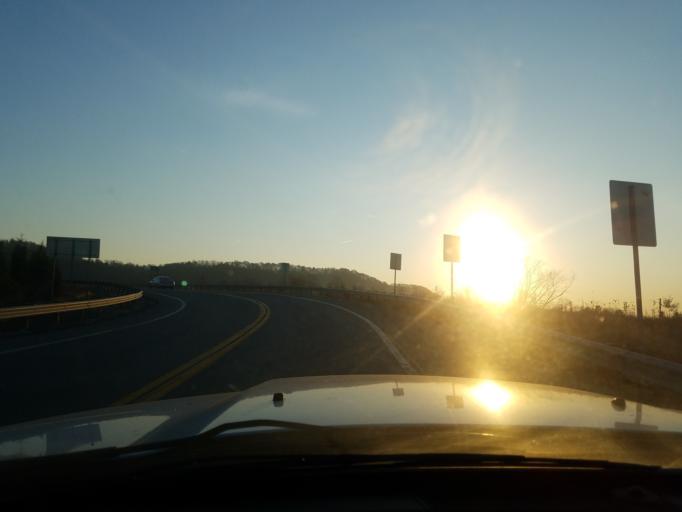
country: US
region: West Virginia
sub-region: Putnam County
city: Buffalo
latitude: 38.5810
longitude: -82.0037
